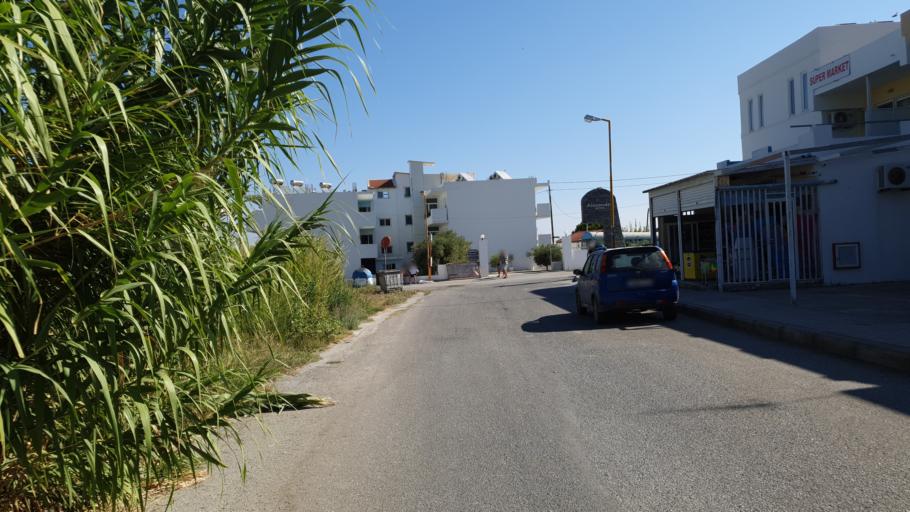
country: GR
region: South Aegean
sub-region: Nomos Dodekanisou
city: Faliraki
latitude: 36.3321
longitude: 28.2073
